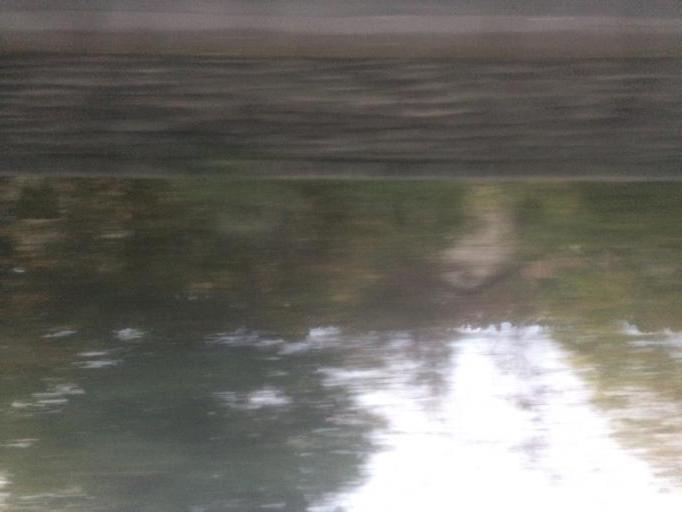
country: GB
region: Scotland
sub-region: Perth and Kinross
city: Perth
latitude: 56.3880
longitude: -3.4764
